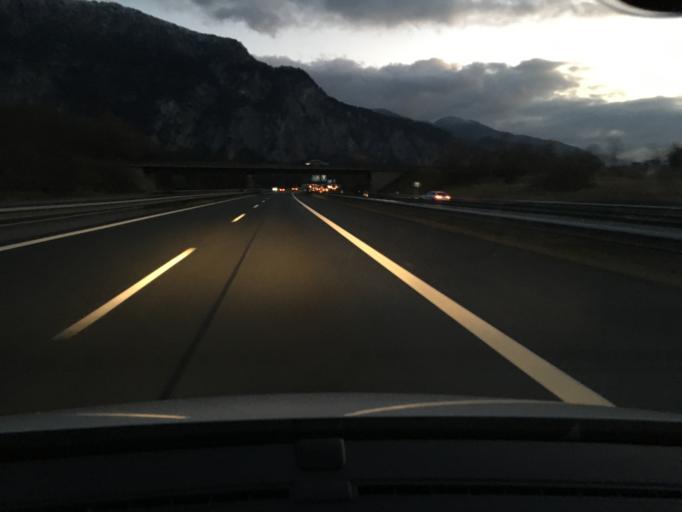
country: DE
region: Bavaria
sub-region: Upper Bavaria
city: Kiefersfelden
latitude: 47.6200
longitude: 12.2021
